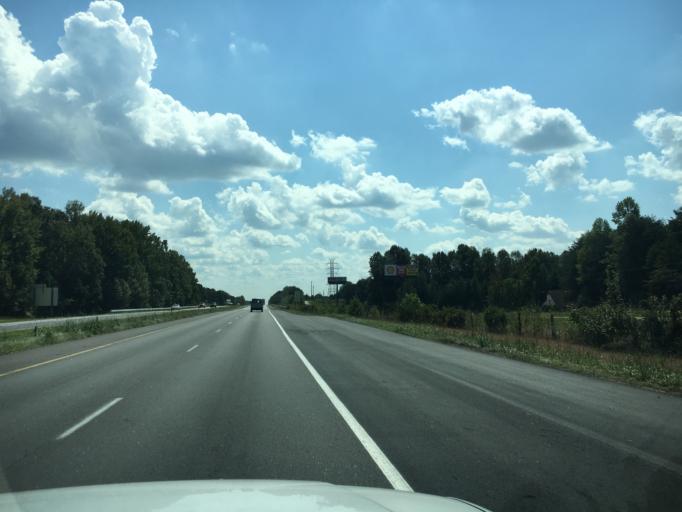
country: US
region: South Carolina
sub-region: Spartanburg County
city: Arcadia
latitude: 34.9155
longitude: -81.9897
